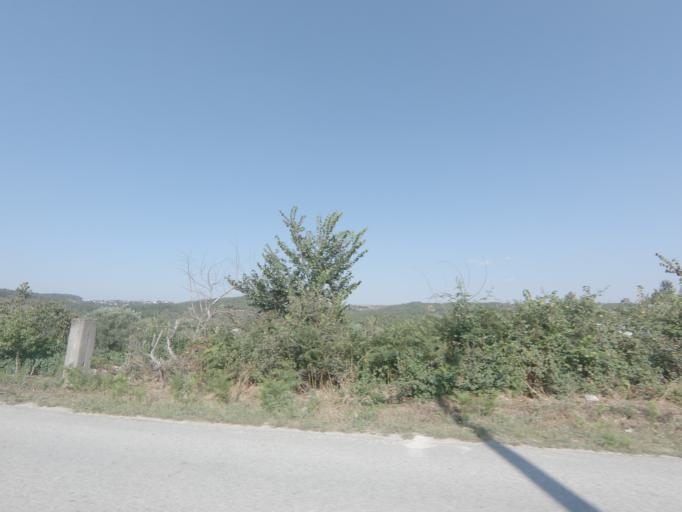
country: PT
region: Viseu
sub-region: Moimenta da Beira
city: Moimenta da Beira
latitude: 40.9740
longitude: -7.5913
